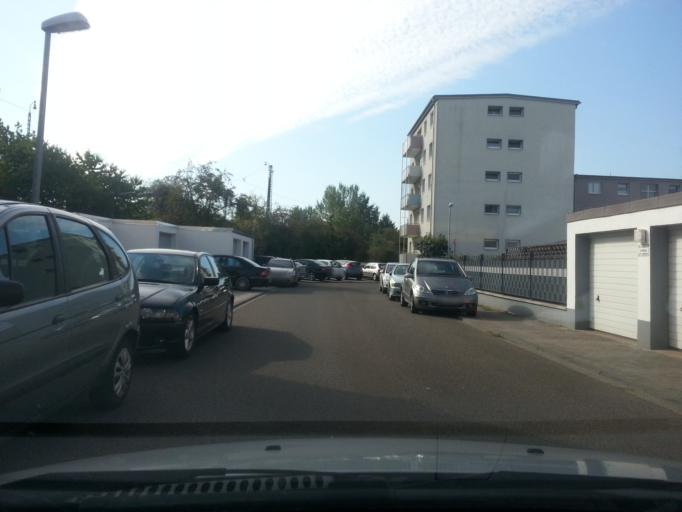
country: DE
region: Rheinland-Pfalz
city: Worms
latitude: 49.6420
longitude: 8.3567
